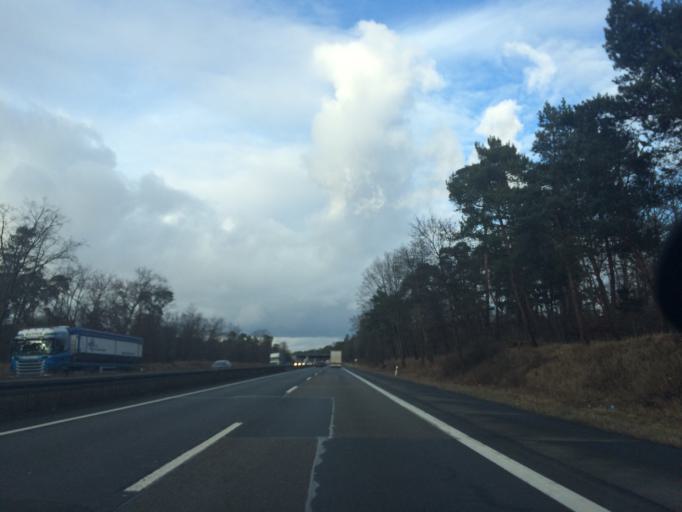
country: DE
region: Hesse
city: Pfungstadt
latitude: 49.8296
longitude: 8.5899
